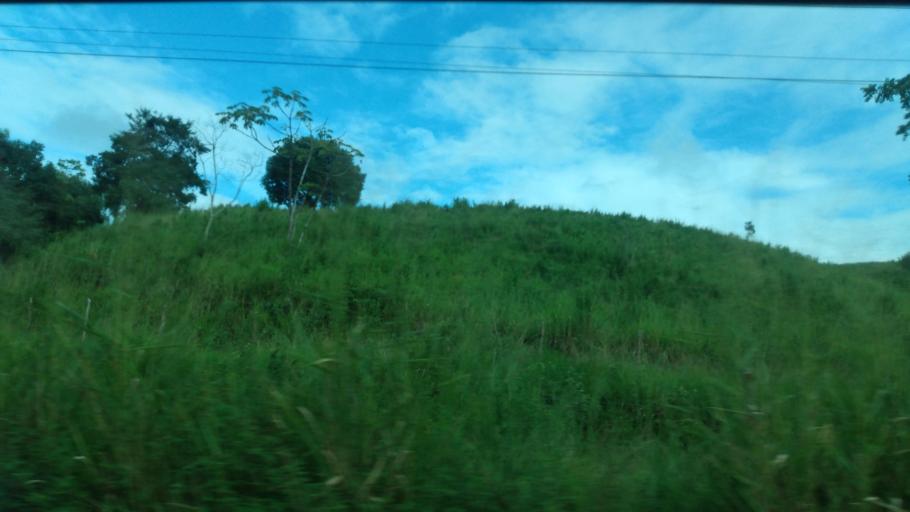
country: BR
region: Pernambuco
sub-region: Catende
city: Catende
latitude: -8.6966
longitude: -35.7333
